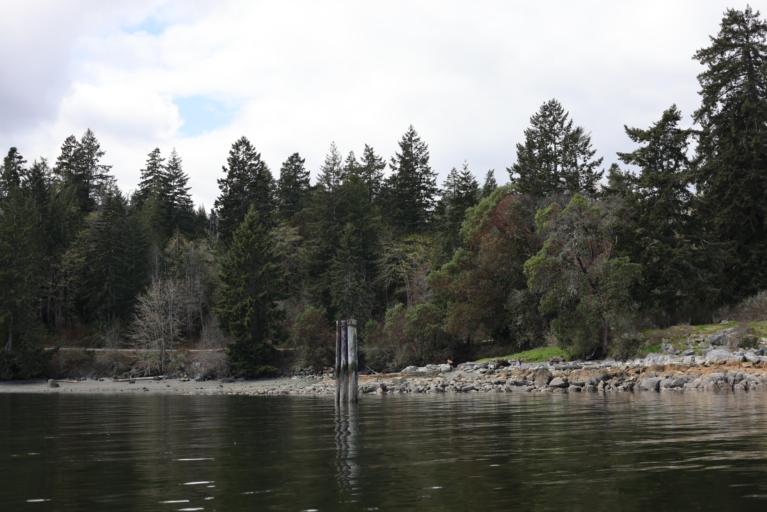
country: CA
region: British Columbia
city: North Saanich
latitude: 48.6317
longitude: -123.5280
